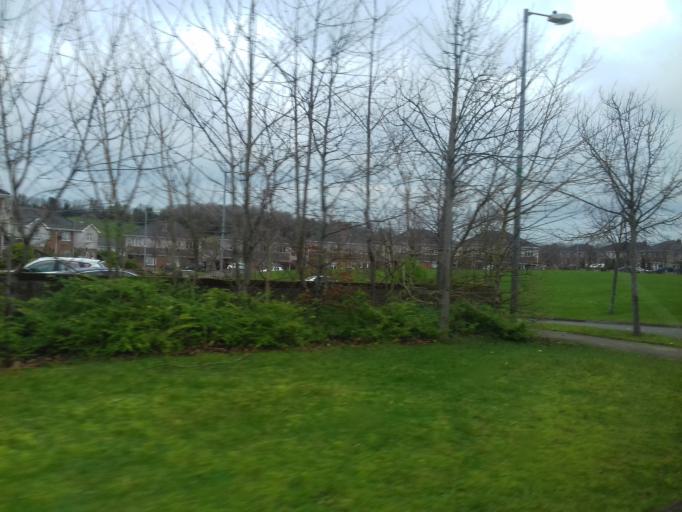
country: IE
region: Leinster
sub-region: An Mhi
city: Duleek
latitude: 53.6907
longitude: -6.4134
